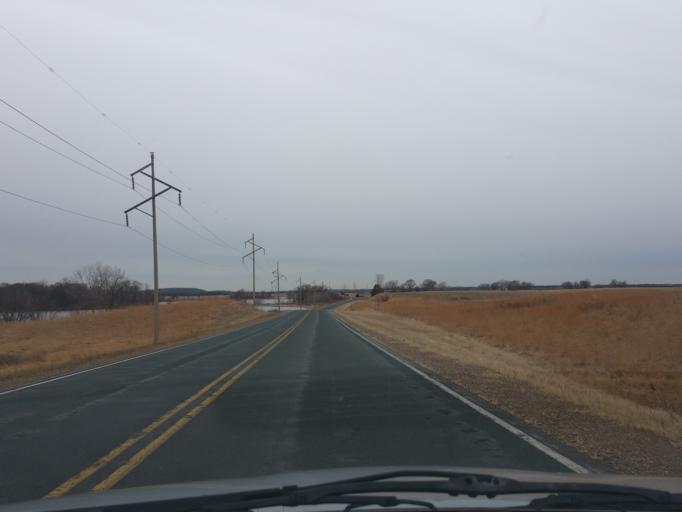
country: US
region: Wisconsin
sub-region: Saint Croix County
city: Roberts
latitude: 45.0357
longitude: -92.5813
